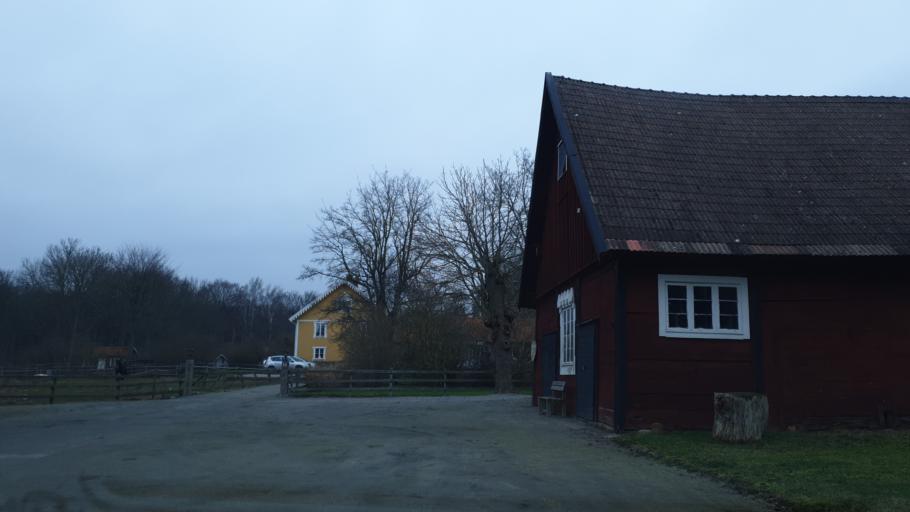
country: SE
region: Blekinge
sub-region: Karlskrona Kommun
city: Rodeby
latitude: 56.2188
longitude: 15.6768
